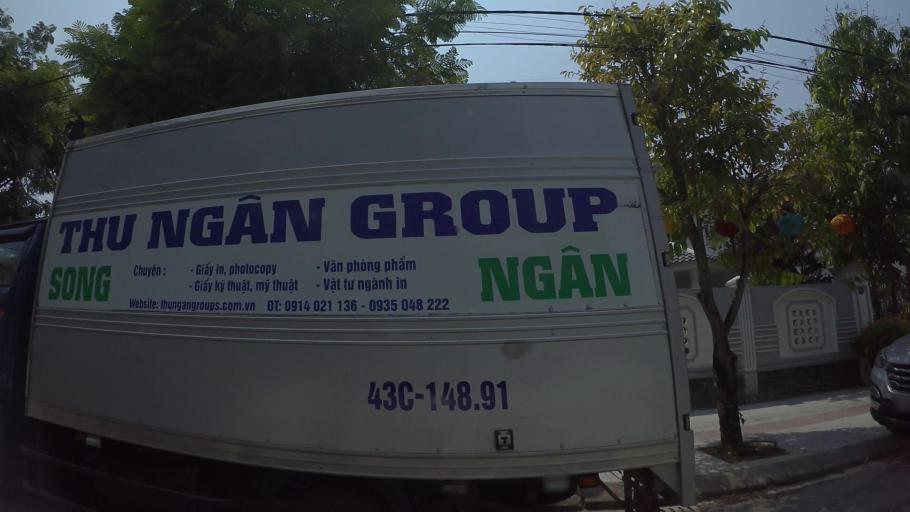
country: VN
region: Da Nang
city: Cam Le
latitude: 16.0207
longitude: 108.2254
